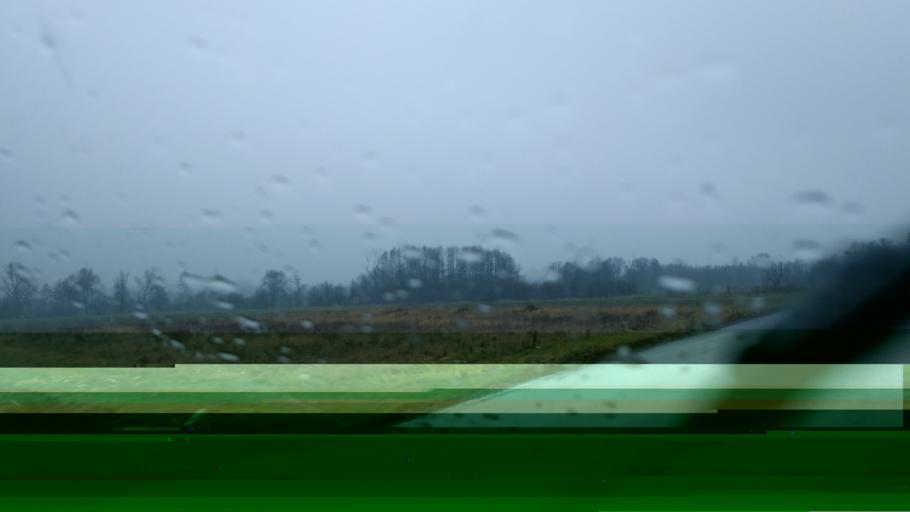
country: PL
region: Subcarpathian Voivodeship
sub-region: Powiat lancucki
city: Krzemienica
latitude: 50.0838
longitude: 22.1632
